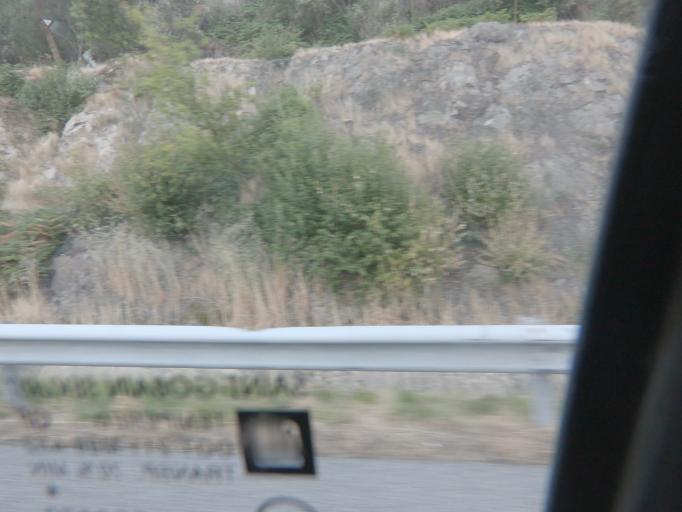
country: PT
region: Porto
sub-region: Marco de Canaveses
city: Marco de Canavezes
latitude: 41.2290
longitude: -8.1295
